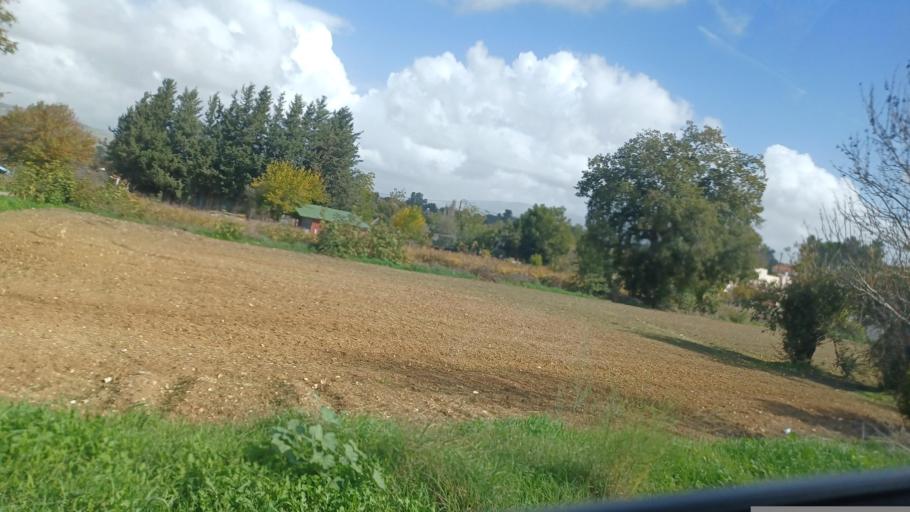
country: CY
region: Pafos
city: Mesogi
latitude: 34.8871
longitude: 32.5049
